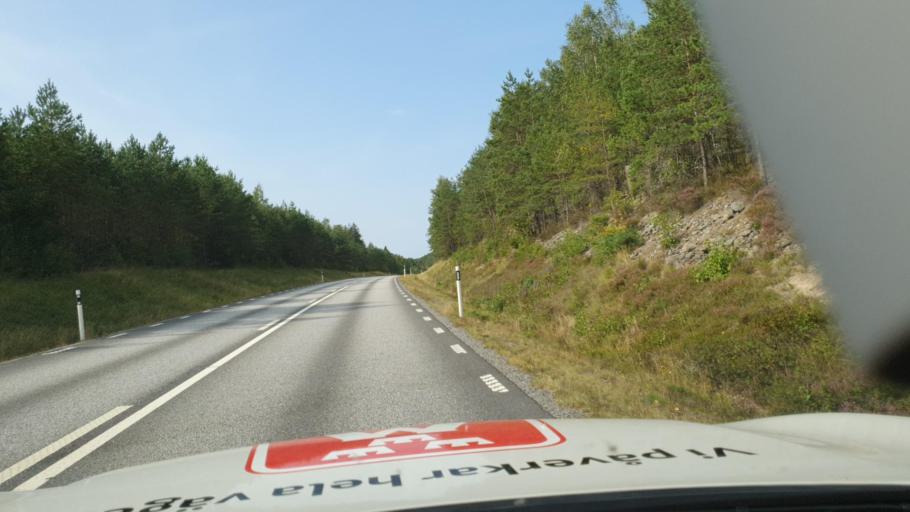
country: SE
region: Vaestra Goetaland
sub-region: Dals-Ed Kommun
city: Ed
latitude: 58.8469
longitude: 11.6770
